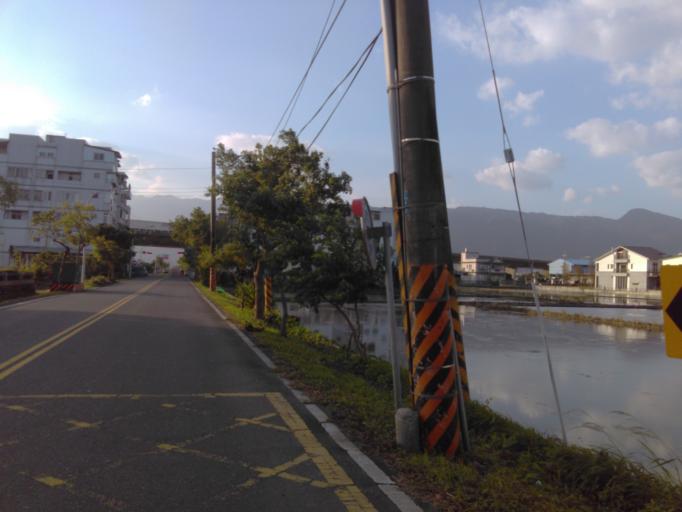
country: TW
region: Taiwan
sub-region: Yilan
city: Yilan
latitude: 24.7999
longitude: 121.7841
